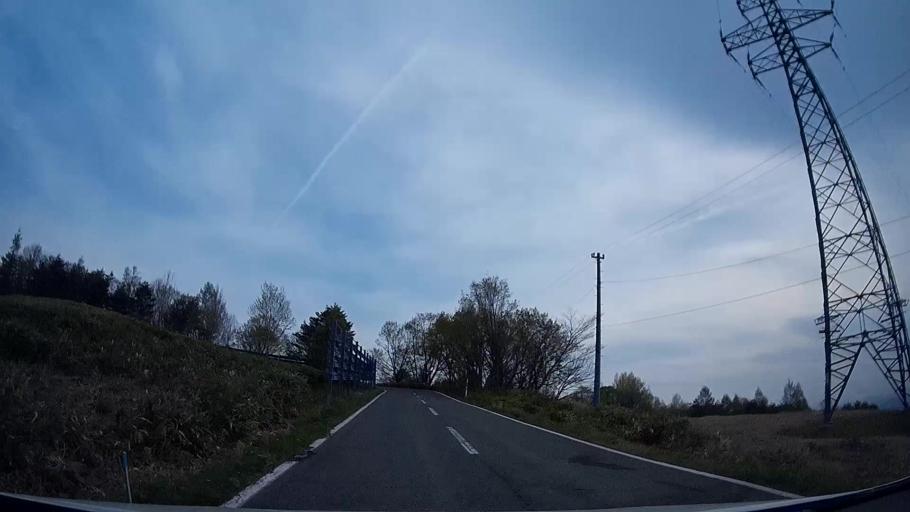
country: JP
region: Iwate
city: Shizukuishi
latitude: 39.9246
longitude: 140.9770
